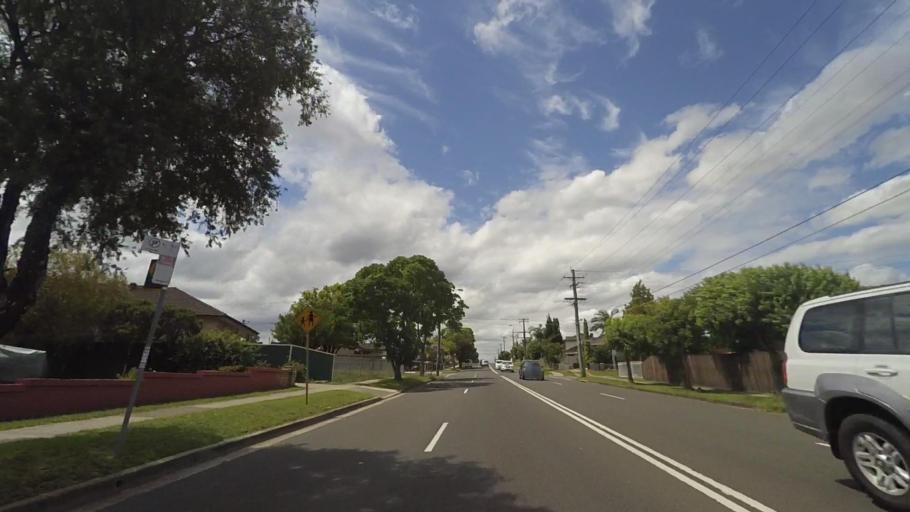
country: AU
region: New South Wales
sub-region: Fairfield
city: Fairfield Heights
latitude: -33.8770
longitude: 150.9429
